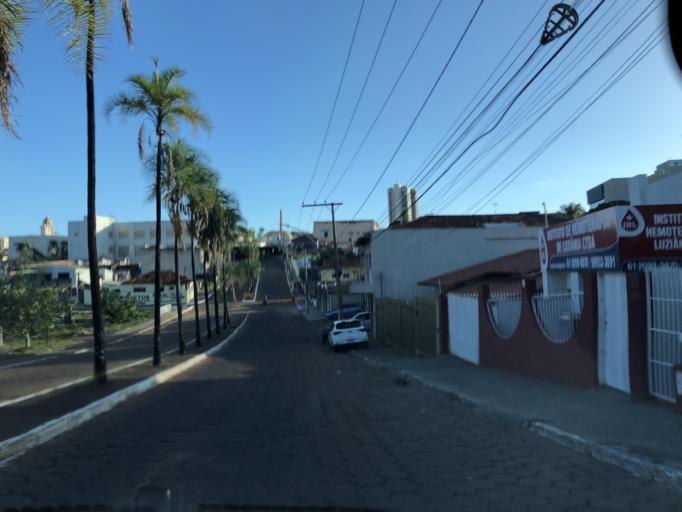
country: BR
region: Goias
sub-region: Luziania
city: Luziania
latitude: -16.2507
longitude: -47.9492
